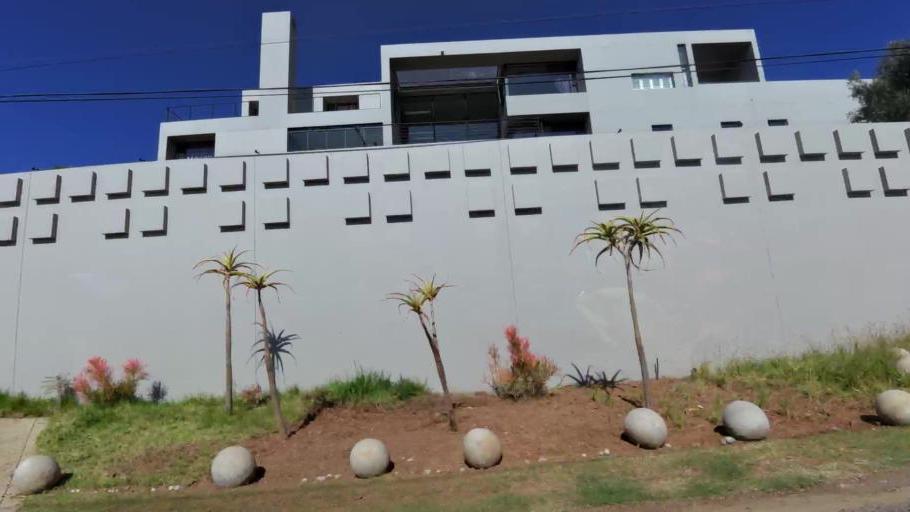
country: ZA
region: Gauteng
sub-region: City of Johannesburg Metropolitan Municipality
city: Roodepoort
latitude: -26.1439
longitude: 27.9649
